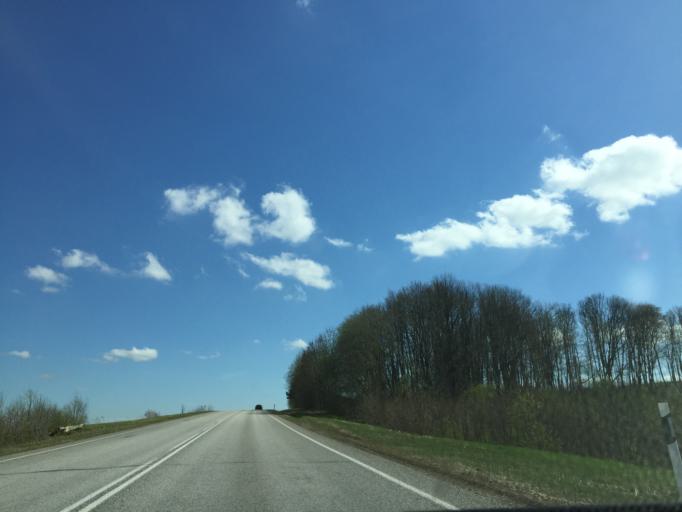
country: EE
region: Valgamaa
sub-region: Valga linn
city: Valga
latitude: 57.9050
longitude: 26.0464
